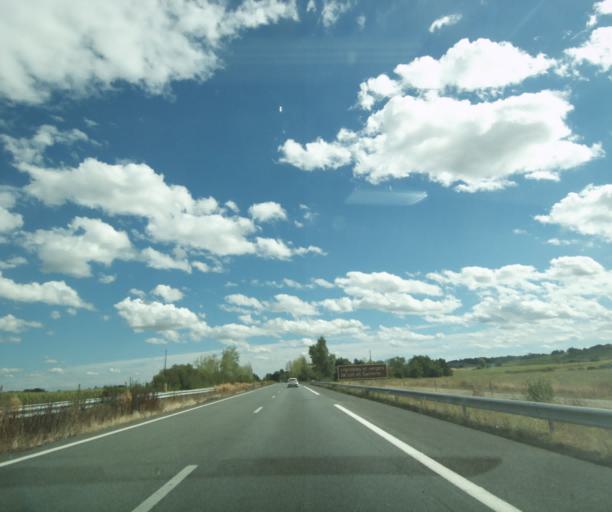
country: FR
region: Aquitaine
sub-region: Departement du Lot-et-Garonne
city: Meilhan-sur-Garonne
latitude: 44.4815
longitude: 0.0159
